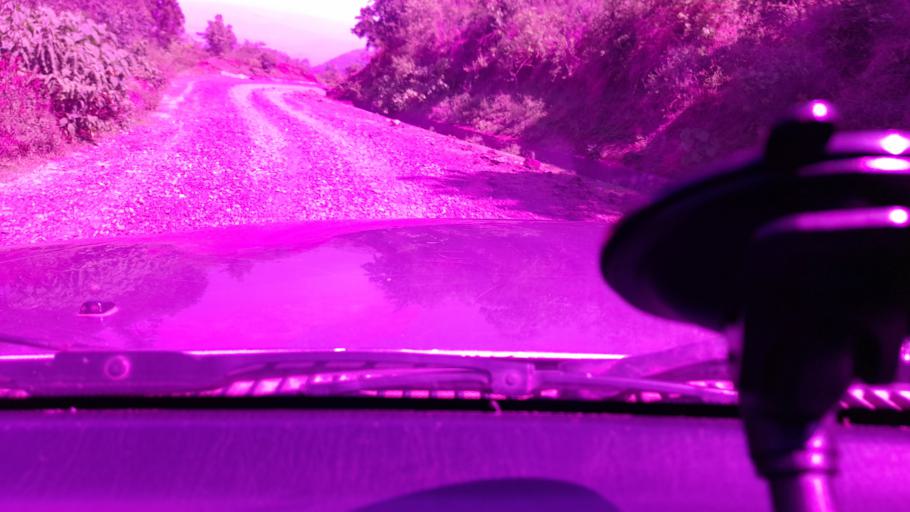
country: ET
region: Oromiya
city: Jima
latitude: 7.8300
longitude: 37.5459
